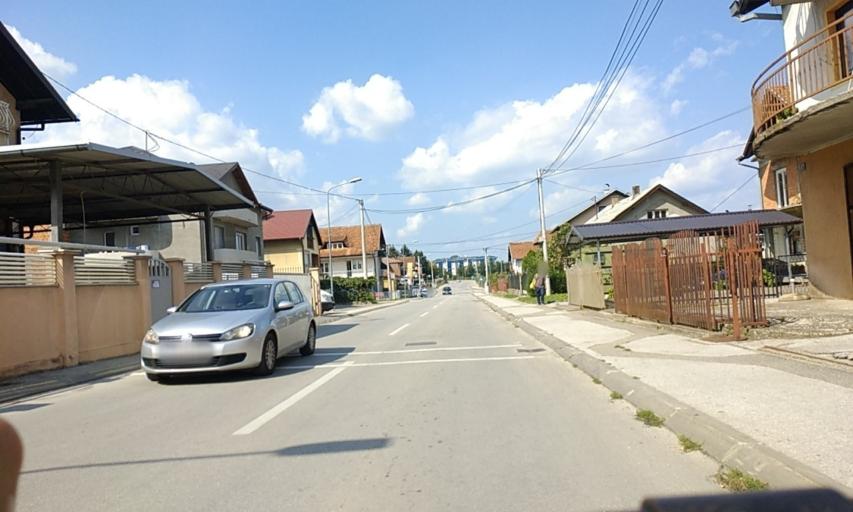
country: BA
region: Republika Srpska
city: Banja Luka
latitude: 44.7896
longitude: 17.1942
